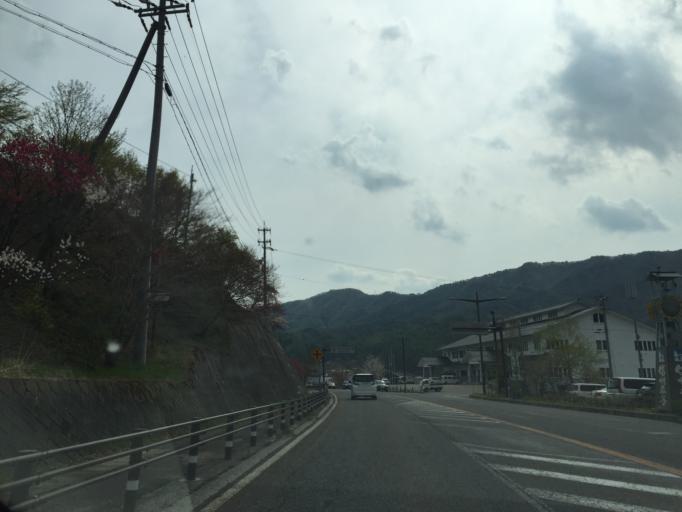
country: JP
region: Gifu
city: Nakatsugawa
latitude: 35.3237
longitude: 137.6316
